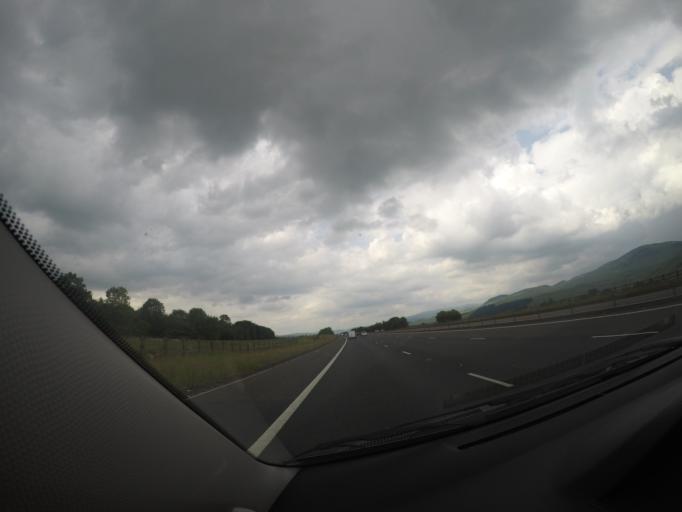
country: GB
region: Scotland
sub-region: Dumfries and Galloway
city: Moffat
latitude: 55.2682
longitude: -3.4181
